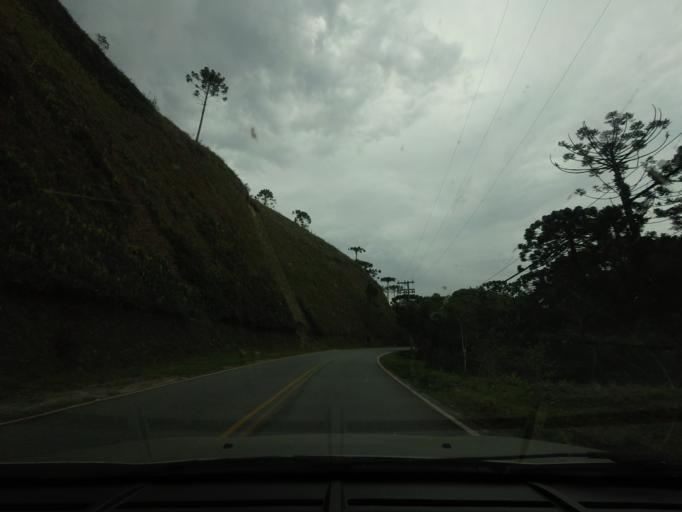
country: BR
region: Sao Paulo
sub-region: Campos Do Jordao
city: Campos do Jordao
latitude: -22.6944
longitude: -45.5131
